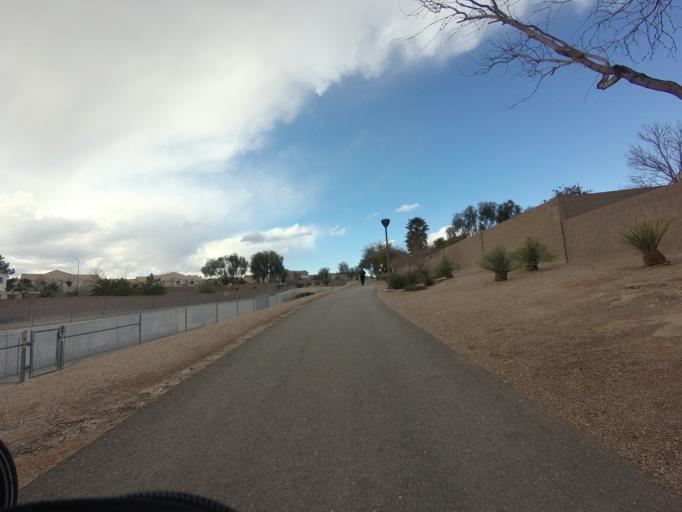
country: US
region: Nevada
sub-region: Clark County
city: North Las Vegas
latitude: 36.2682
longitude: -115.1968
